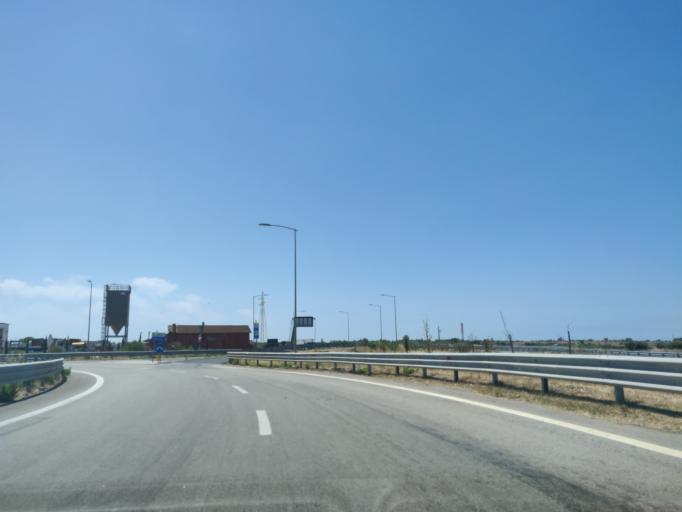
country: IT
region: Latium
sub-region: Citta metropolitana di Roma Capitale
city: Aurelia
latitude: 42.1641
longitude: 11.7883
